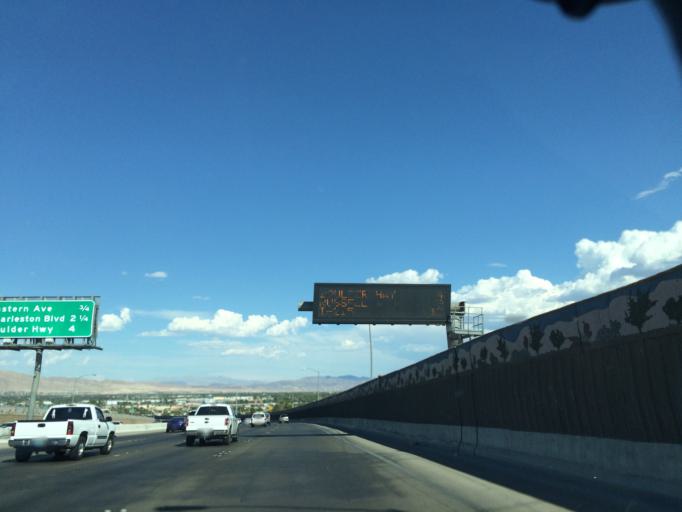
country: US
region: Nevada
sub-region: Clark County
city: Las Vegas
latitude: 36.1693
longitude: -115.1284
